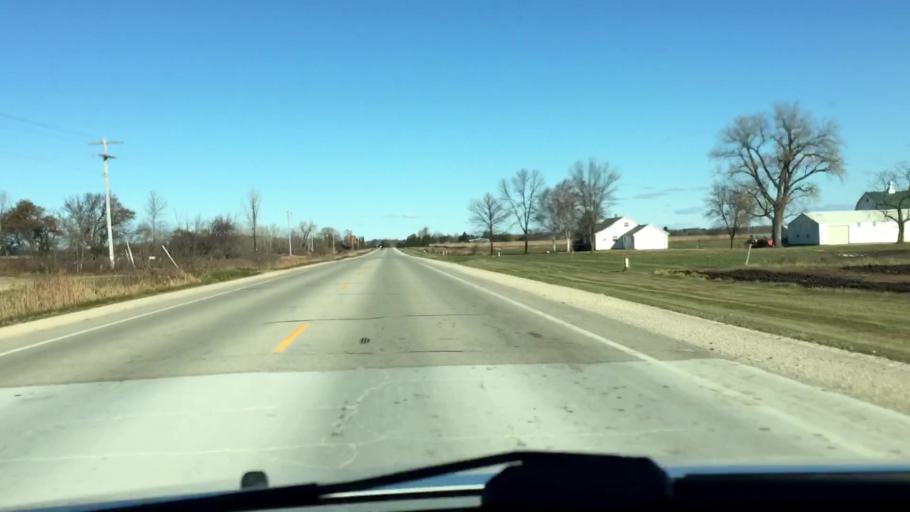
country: US
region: Wisconsin
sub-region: Brown County
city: Pulaski
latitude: 44.7335
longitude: -88.2473
